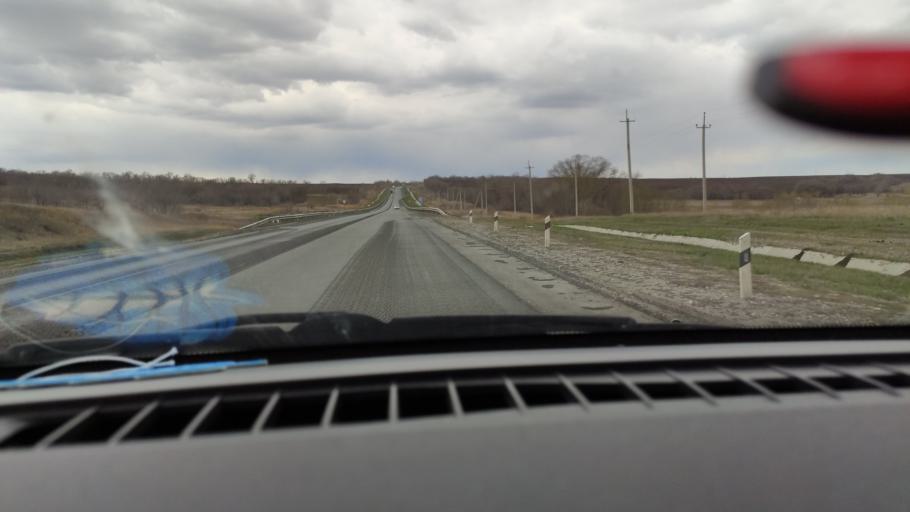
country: RU
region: Saratov
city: Shumeyka
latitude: 51.7816
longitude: 46.1271
